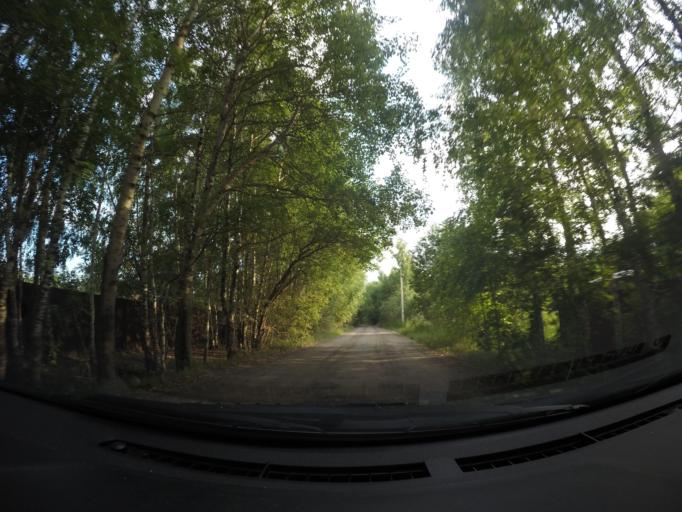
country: RU
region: Moskovskaya
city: Krasnyy Tkach
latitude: 55.4238
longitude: 39.2388
